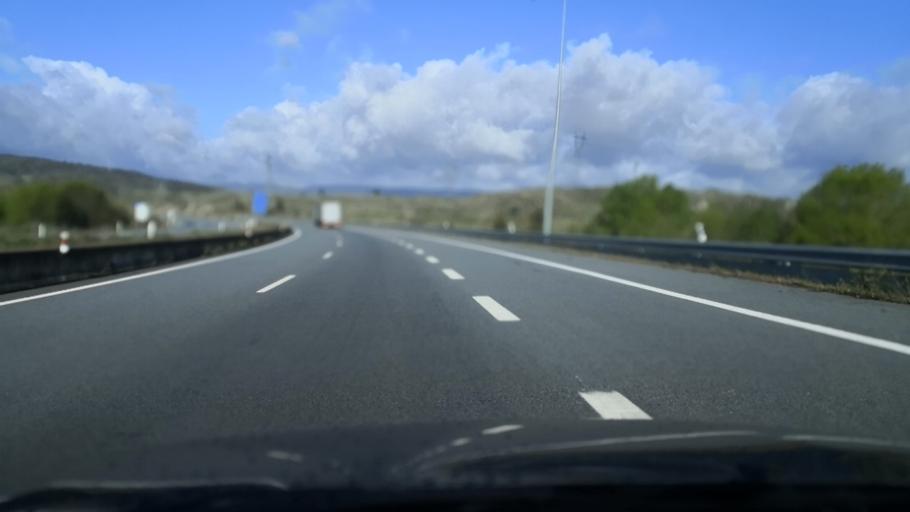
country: PT
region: Guarda
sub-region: Celorico da Beira
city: Celorico da Beira
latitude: 40.6305
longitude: -7.4167
